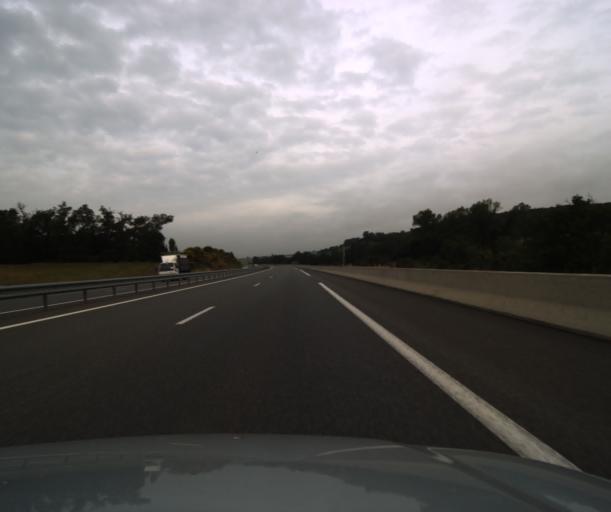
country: FR
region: Midi-Pyrenees
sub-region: Departement du Gers
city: Aubiet
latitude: 43.6583
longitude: 0.7750
